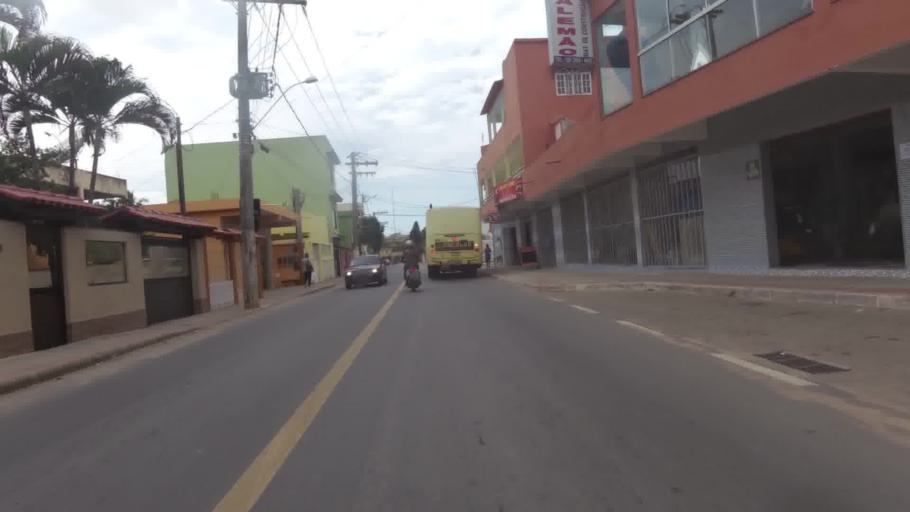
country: BR
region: Espirito Santo
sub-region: Piuma
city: Piuma
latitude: -20.8395
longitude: -40.7312
